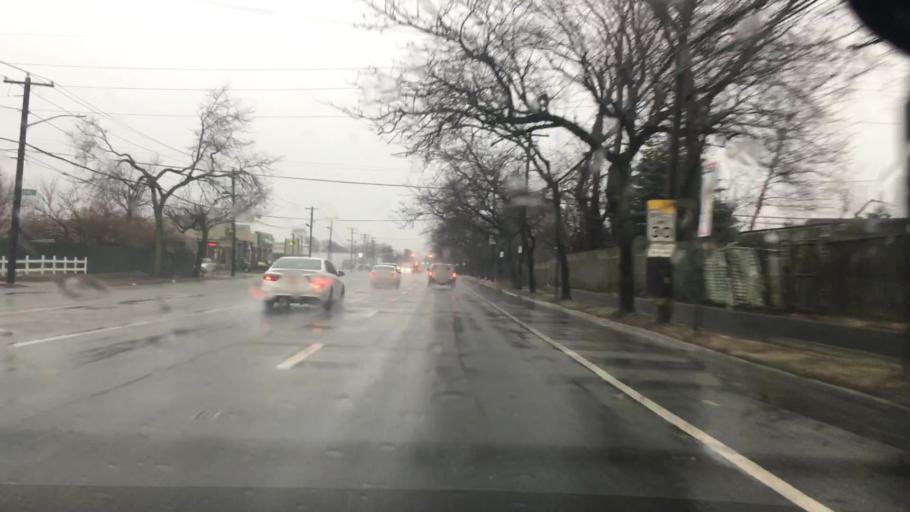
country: US
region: New York
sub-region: Nassau County
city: Hicksville
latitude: 40.7583
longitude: -73.5408
